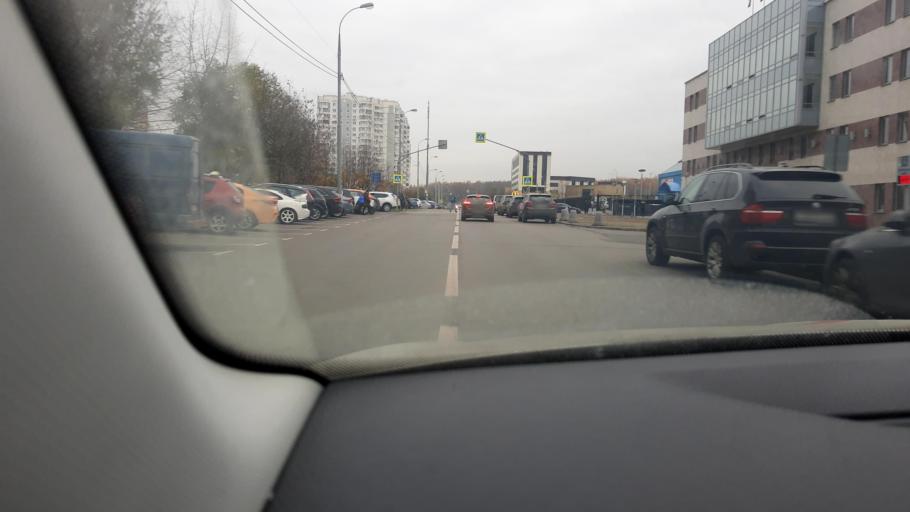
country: RU
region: Moskovskaya
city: Shcherbinka
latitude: 55.5470
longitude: 37.5421
